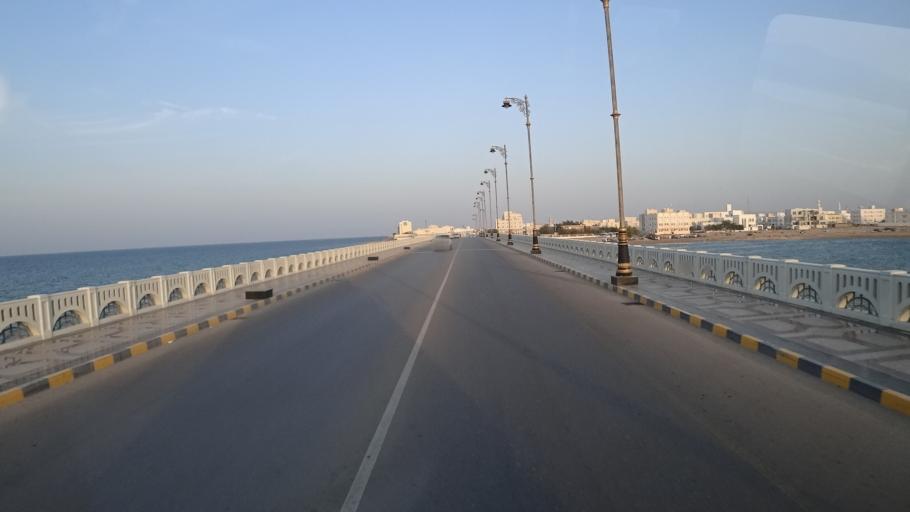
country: OM
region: Ash Sharqiyah
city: Sur
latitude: 22.5973
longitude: 59.4889
